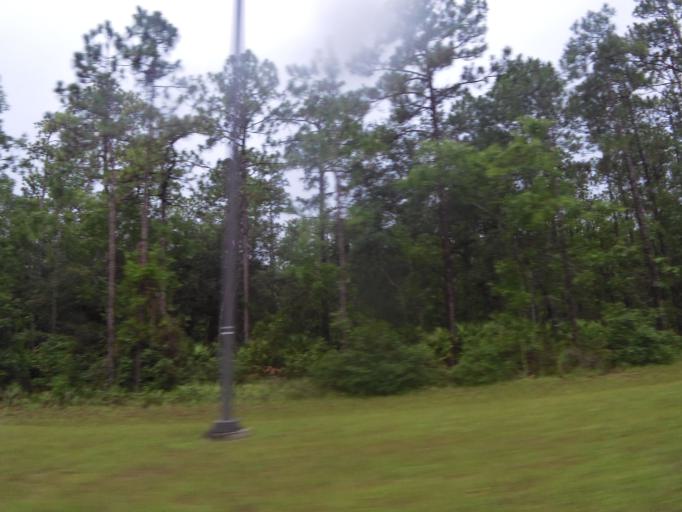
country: US
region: Florida
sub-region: Duval County
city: Jacksonville Beach
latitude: 30.2632
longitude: -81.4995
